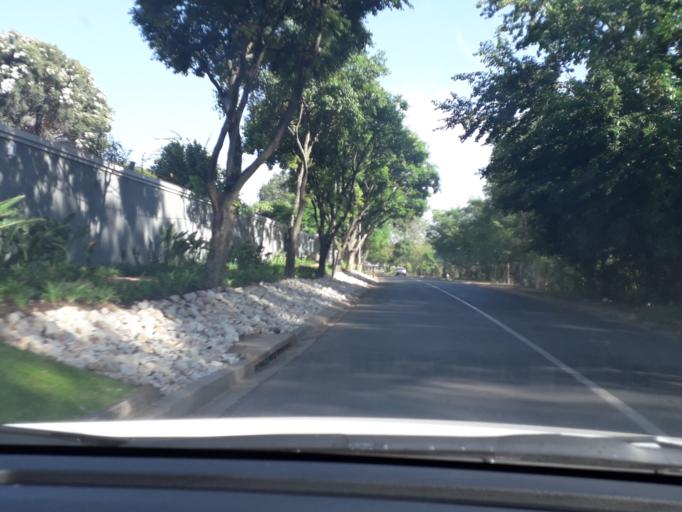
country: ZA
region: Gauteng
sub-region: City of Johannesburg Metropolitan Municipality
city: Diepsloot
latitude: -26.0360
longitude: 27.9851
